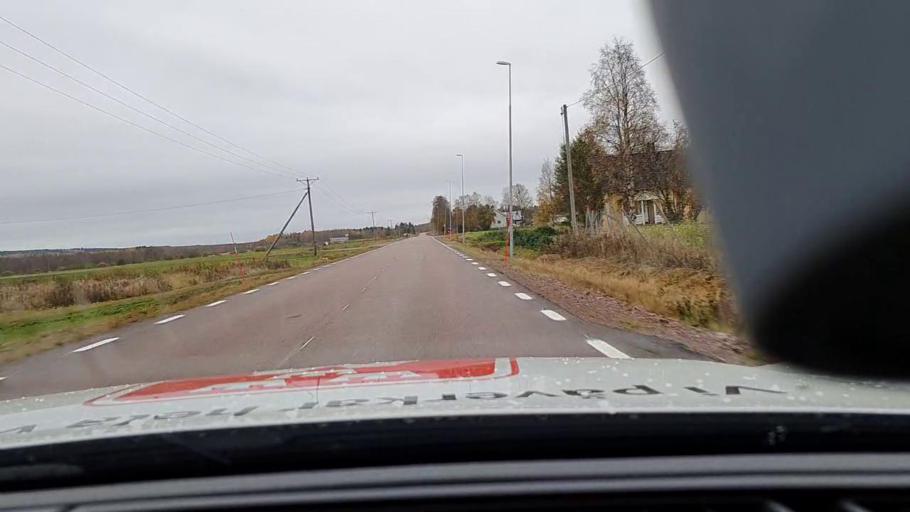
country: FI
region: Lapland
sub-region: Torniolaakso
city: Ylitornio
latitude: 66.1360
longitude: 23.9036
